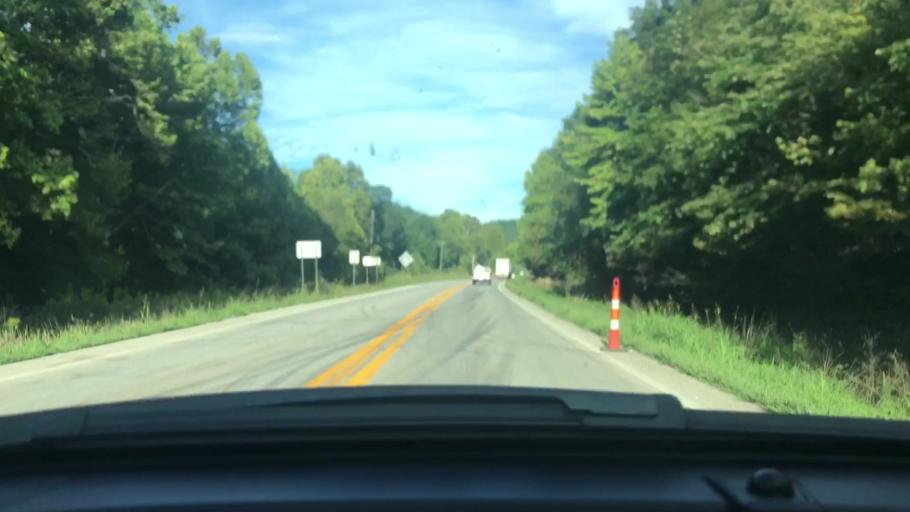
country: US
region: Arkansas
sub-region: Sharp County
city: Cherokee Village
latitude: 36.3033
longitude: -91.4252
